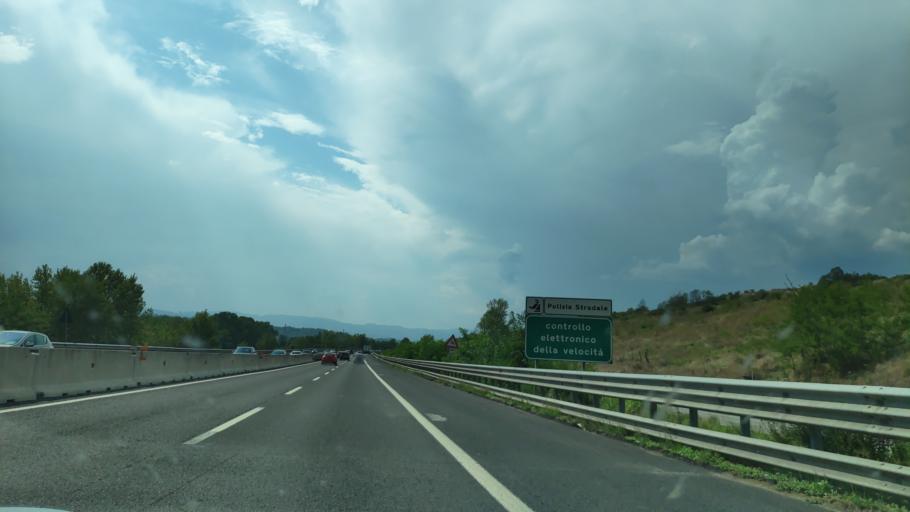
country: IT
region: Tuscany
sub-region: Province of Arezzo
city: Bucine
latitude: 43.5147
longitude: 11.6215
